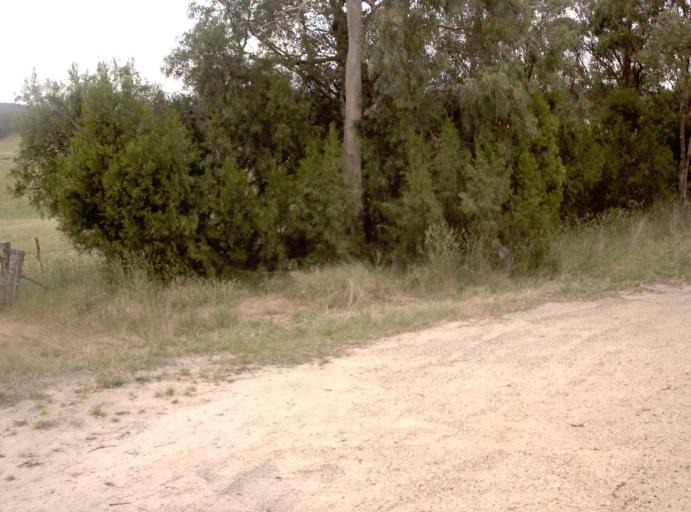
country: AU
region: Victoria
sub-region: East Gippsland
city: Bairnsdale
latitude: -37.7797
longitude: 147.5975
